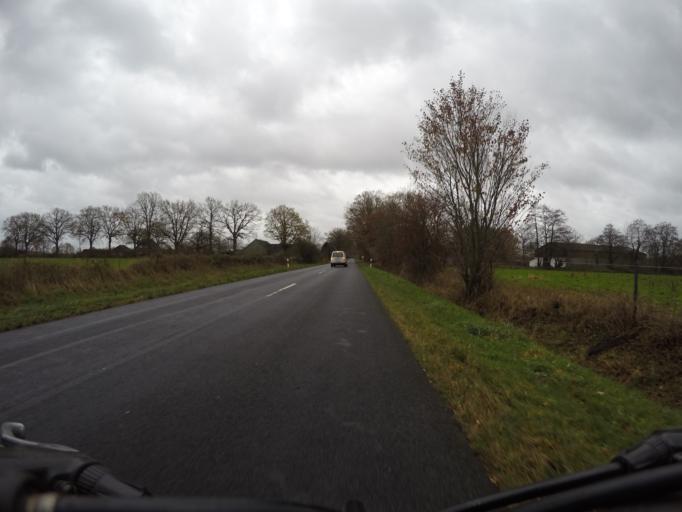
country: DE
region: Schleswig-Holstein
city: Hasloh
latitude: 53.7086
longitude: 9.8806
